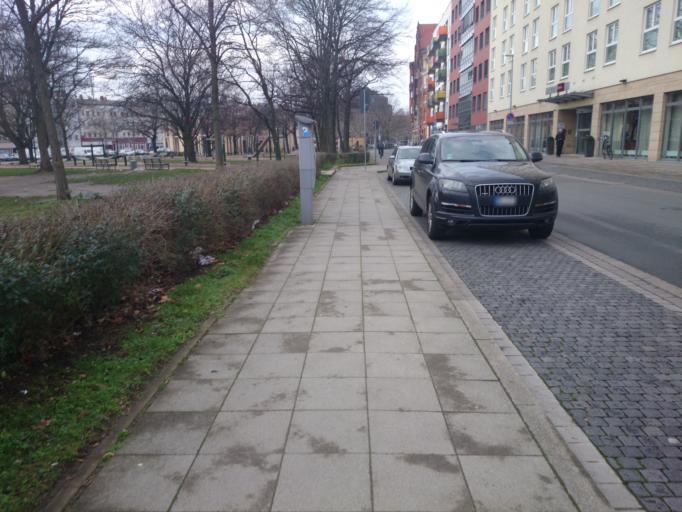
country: DE
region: Lower Saxony
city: Hannover
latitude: 52.3800
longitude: 9.7309
